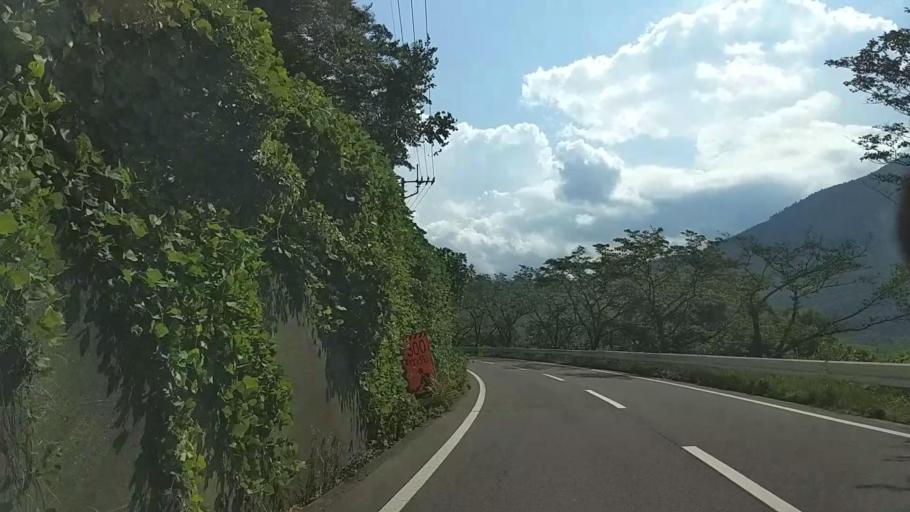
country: JP
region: Shizuoka
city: Fujinomiya
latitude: 35.4023
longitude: 138.4519
